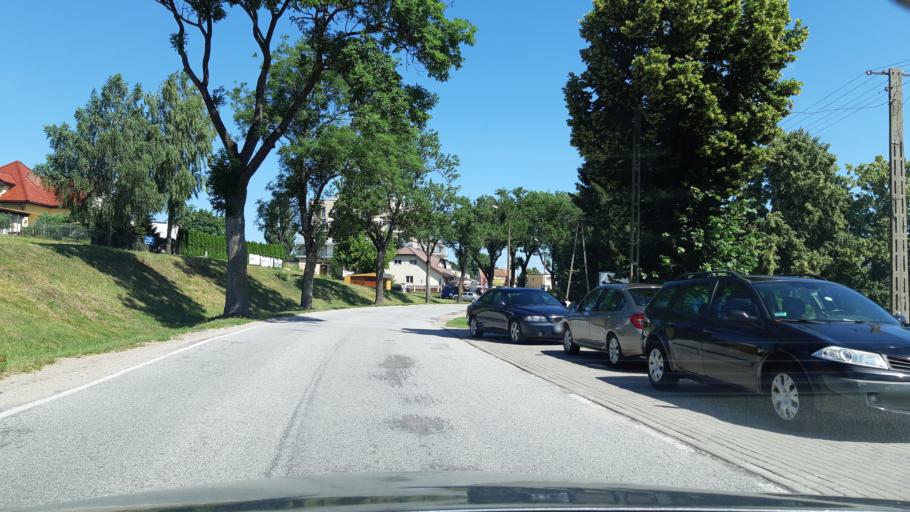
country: PL
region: Warmian-Masurian Voivodeship
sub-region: Powiat gizycki
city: Gizycko
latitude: 54.0099
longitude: 21.7354
